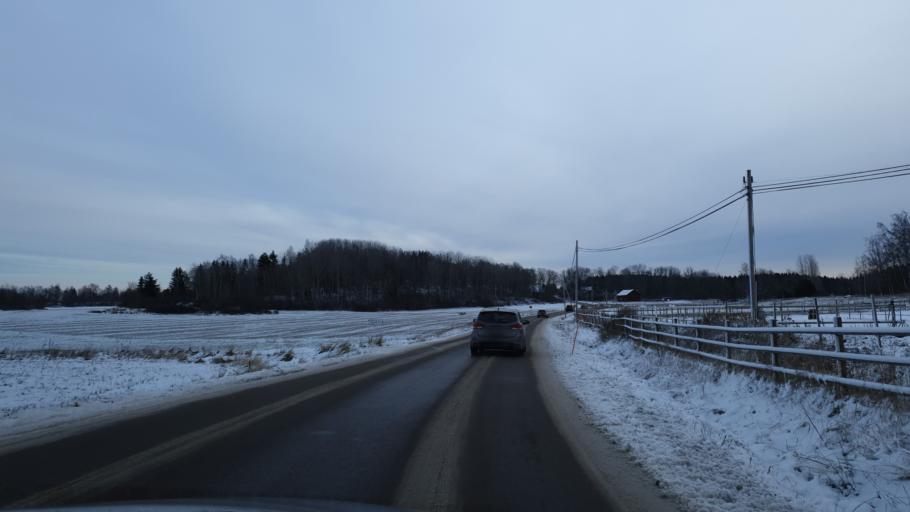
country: SE
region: Uppsala
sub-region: Habo Kommun
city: Balsta
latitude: 59.7087
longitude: 17.5892
